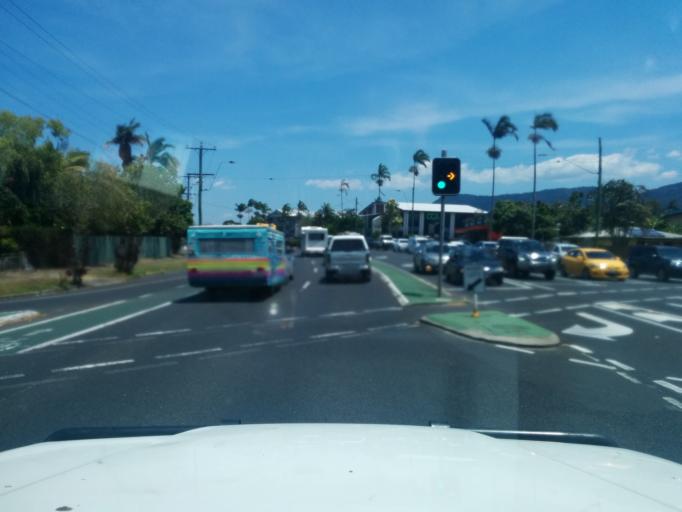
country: AU
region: Queensland
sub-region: Cairns
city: Cairns
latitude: -16.9227
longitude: 145.7401
